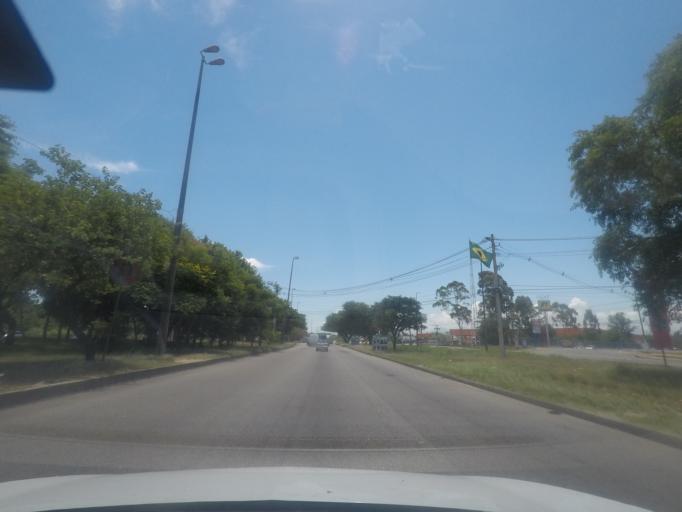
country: BR
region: Rio de Janeiro
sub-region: Itaguai
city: Itaguai
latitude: -22.8932
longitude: -43.6744
